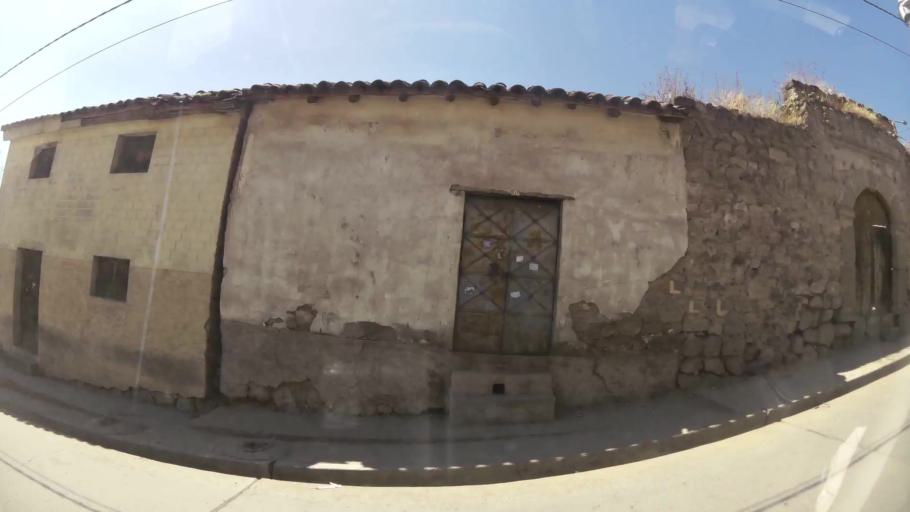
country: PE
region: Ayacucho
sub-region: Provincia de Huamanga
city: Carmen Alto
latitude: -13.1761
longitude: -74.2262
